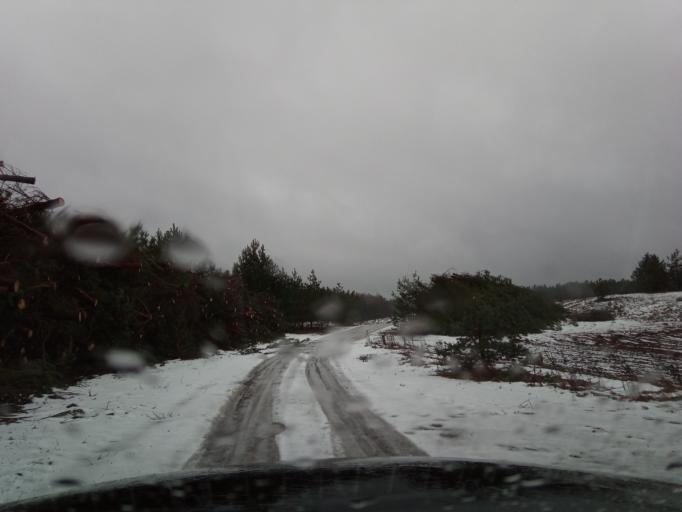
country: LT
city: Svencioneliai
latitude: 55.3414
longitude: 25.8451
